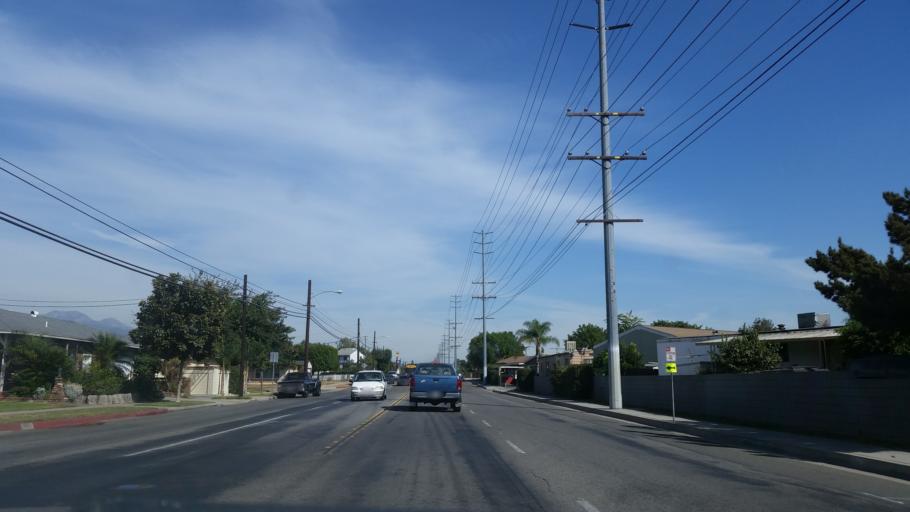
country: US
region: California
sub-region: Los Angeles County
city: Azusa
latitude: 34.1142
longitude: -117.9130
